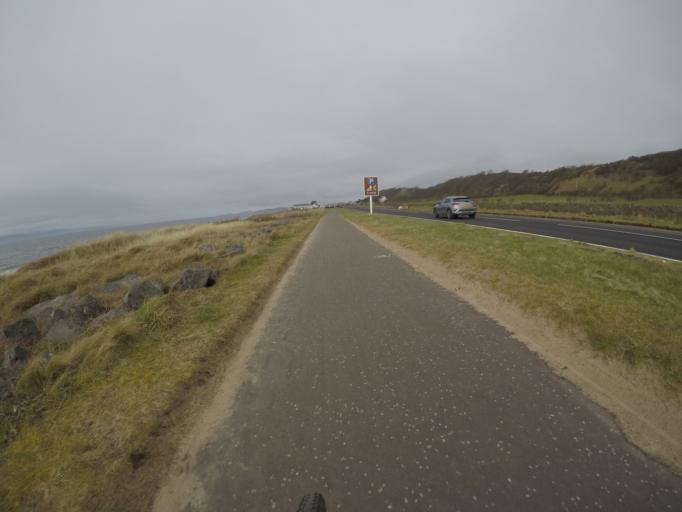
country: GB
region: Scotland
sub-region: North Ayrshire
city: West Kilbride
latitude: 55.6635
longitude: -4.8351
